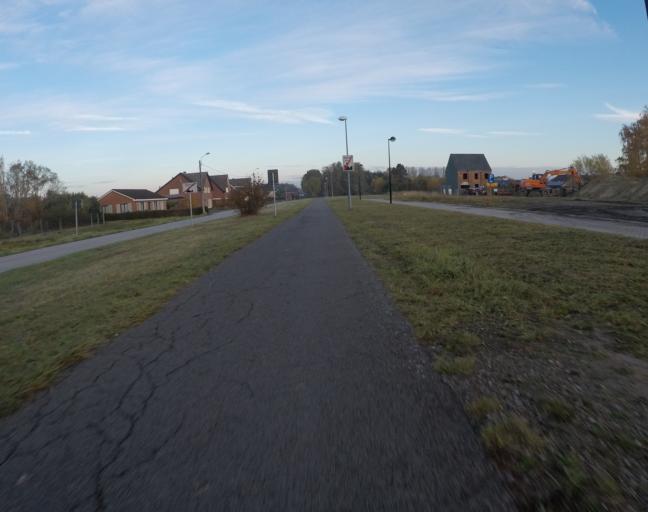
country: BE
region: Flanders
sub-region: Provincie Vlaams-Brabant
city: Begijnendijk
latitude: 51.0320
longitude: 4.8259
